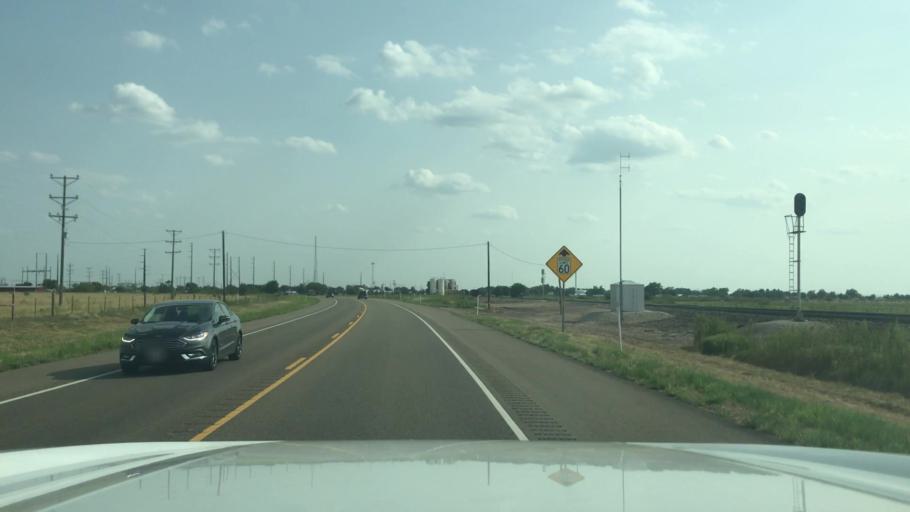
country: US
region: Texas
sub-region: Hartley County
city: Channing
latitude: 35.6956
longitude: -102.3279
